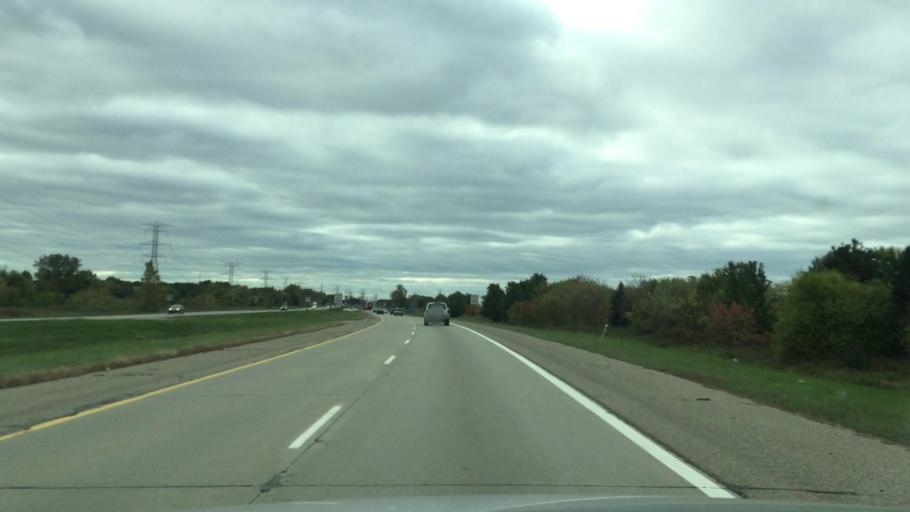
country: US
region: Michigan
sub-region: Macomb County
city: Romeo
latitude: 42.7780
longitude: -83.0096
